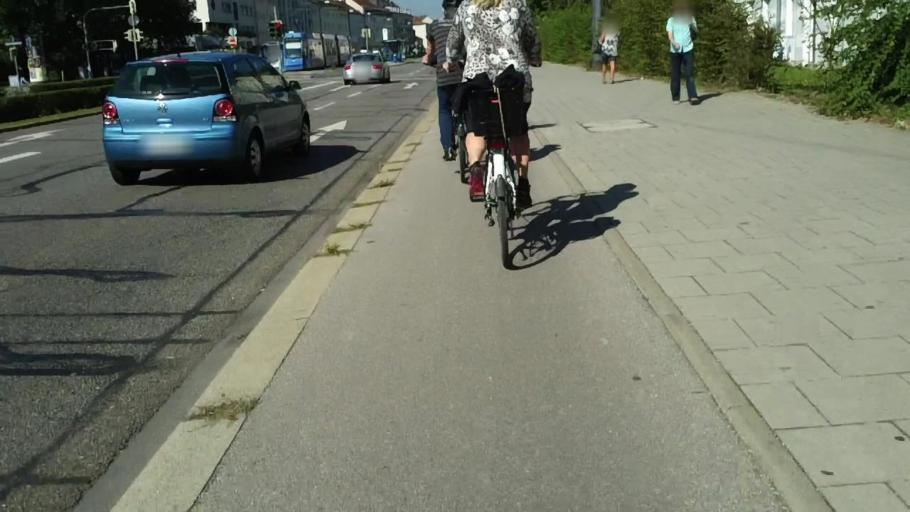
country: DE
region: Bavaria
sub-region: Upper Bavaria
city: Karlsfeld
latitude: 48.1790
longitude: 11.5159
